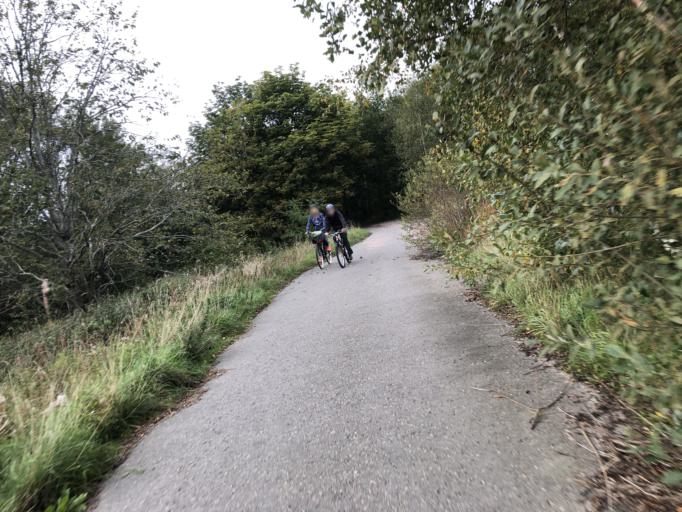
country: SE
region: Vaestra Goetaland
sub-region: Goteborg
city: Majorna
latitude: 57.7566
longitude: 11.9028
